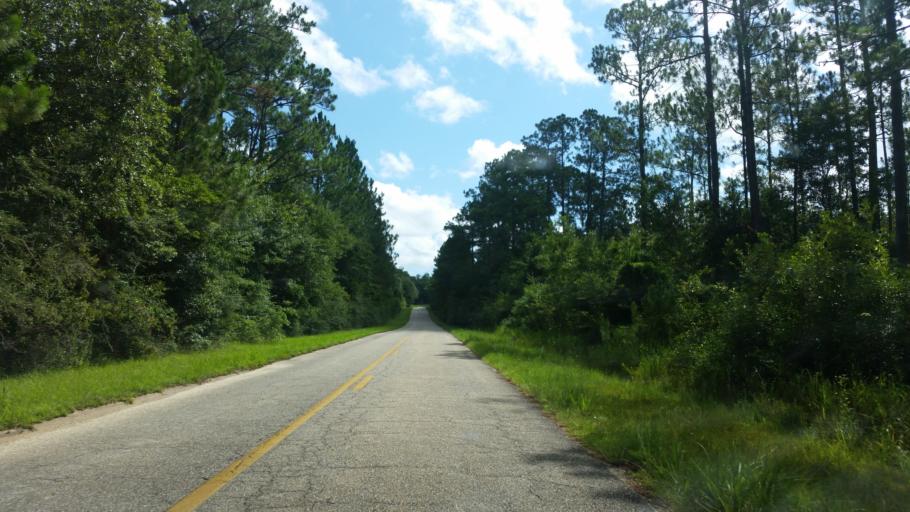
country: US
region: Florida
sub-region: Santa Rosa County
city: Point Baker
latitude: 30.7283
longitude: -86.8966
